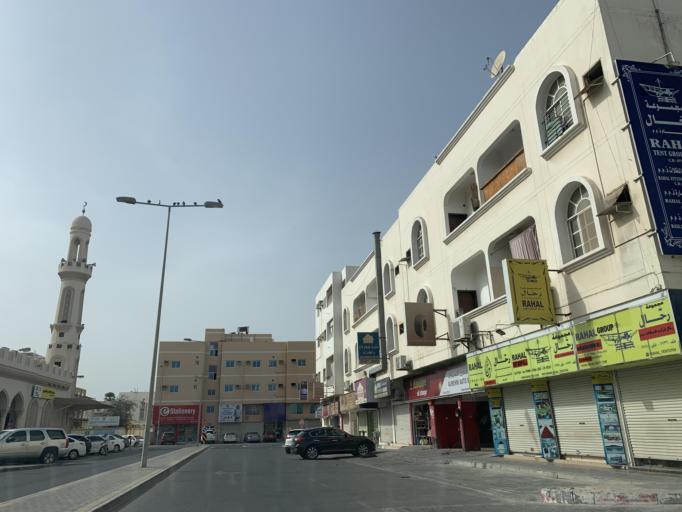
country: BH
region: Northern
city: Ar Rifa'
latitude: 26.1298
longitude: 50.5724
